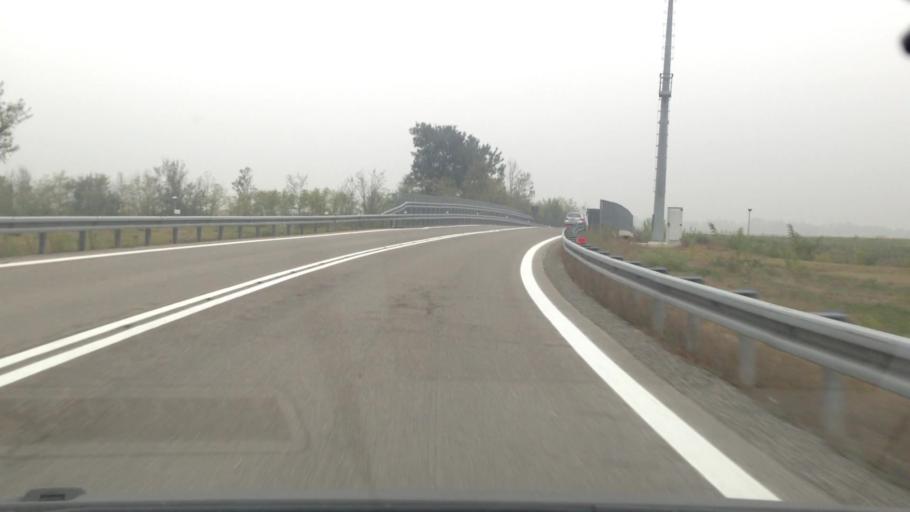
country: IT
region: Piedmont
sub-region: Provincia di Alessandria
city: Quattordio
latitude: 44.9088
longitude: 8.4069
